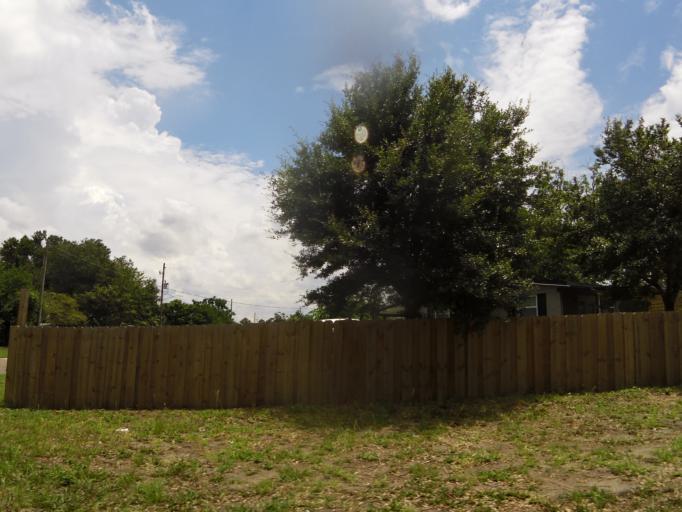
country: US
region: Florida
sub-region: Duval County
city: Atlantic Beach
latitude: 30.3348
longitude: -81.4114
